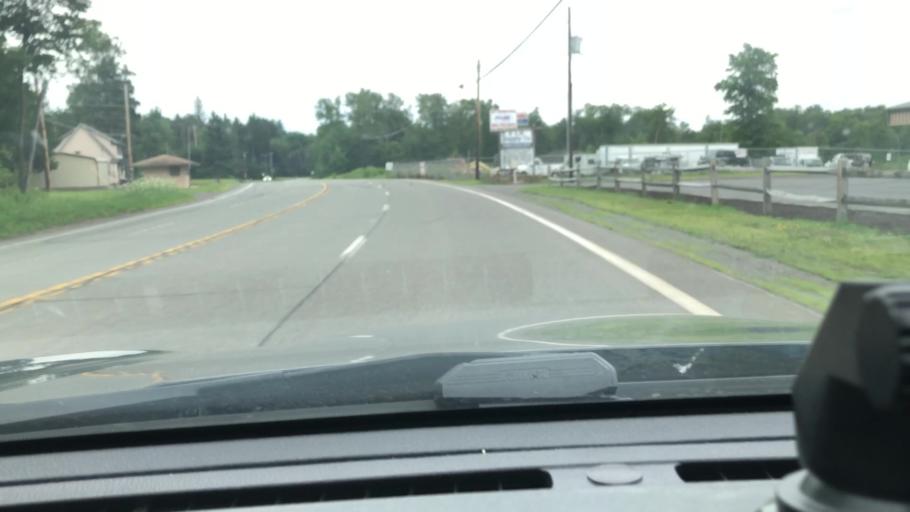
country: US
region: Pennsylvania
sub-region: Lackawanna County
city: Moscow
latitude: 41.2479
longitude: -75.5029
